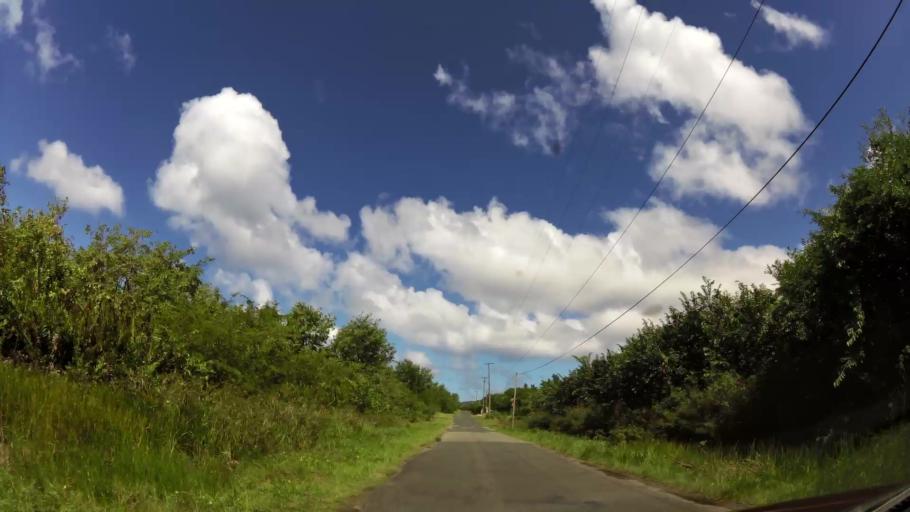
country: DM
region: Saint John
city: Portsmouth
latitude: 15.5870
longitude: -61.4640
